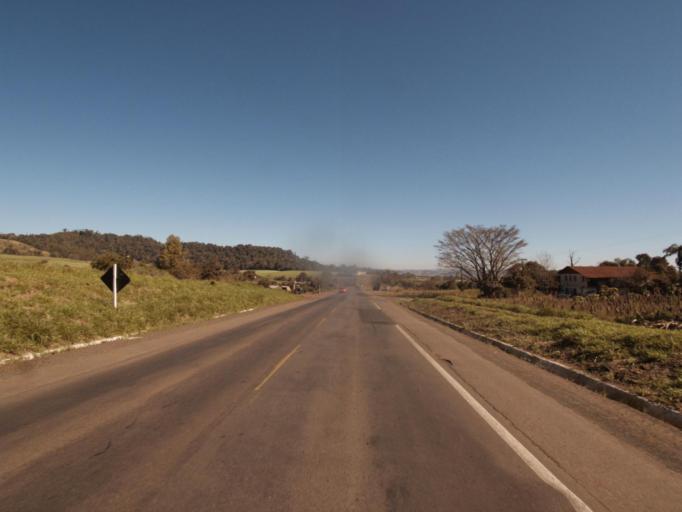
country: BR
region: Rio Grande do Sul
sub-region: Frederico Westphalen
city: Frederico Westphalen
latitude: -26.7997
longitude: -53.3503
